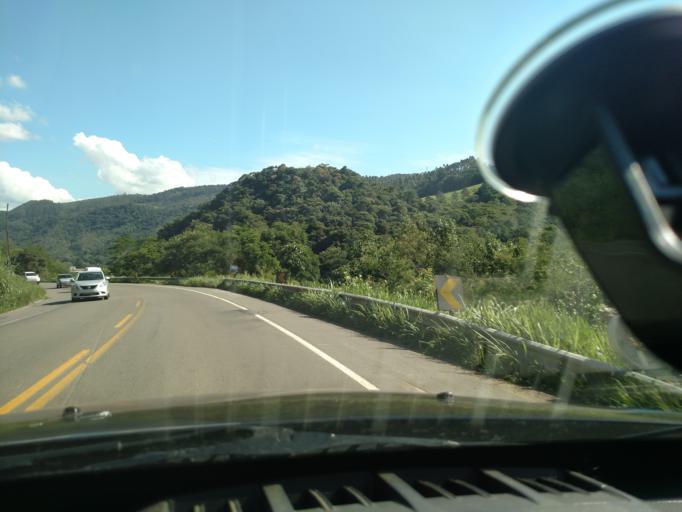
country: BR
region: Santa Catarina
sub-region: Ibirama
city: Ibirama
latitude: -27.0893
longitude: -49.4588
